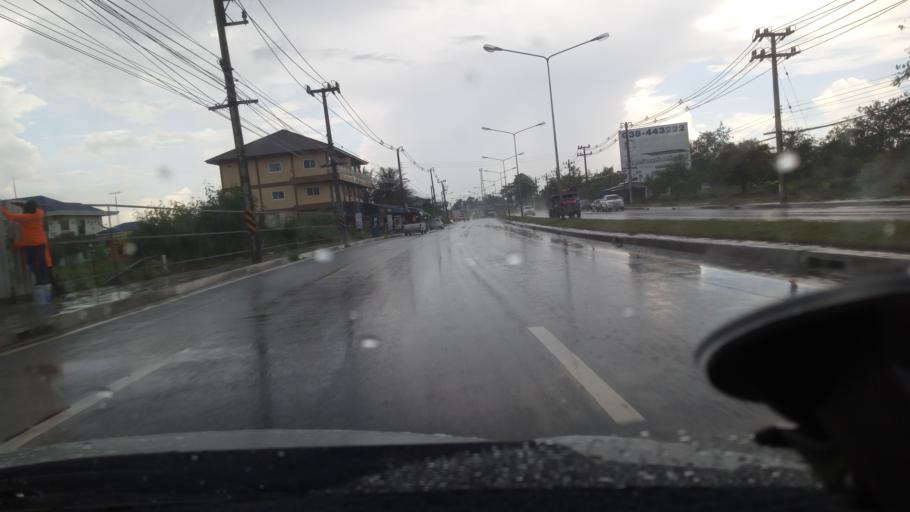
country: TH
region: Chon Buri
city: Phan Thong
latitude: 13.4293
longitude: 101.1091
